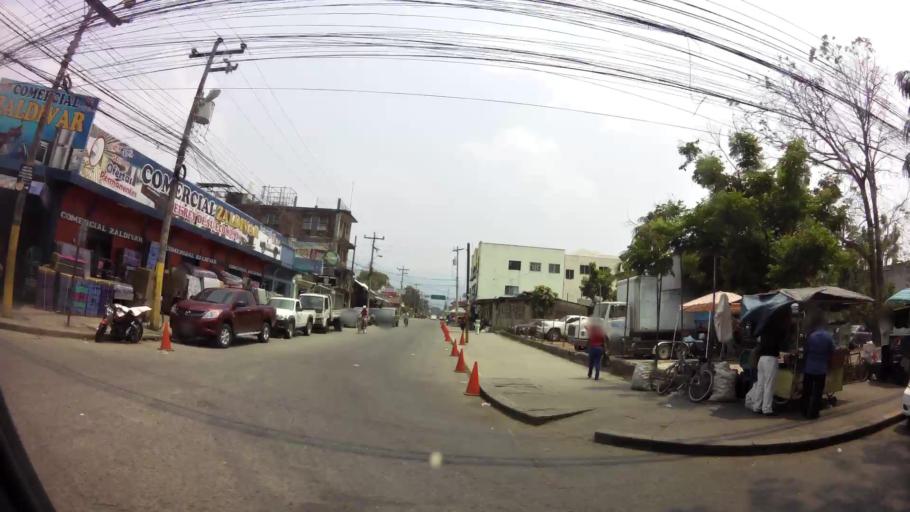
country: HN
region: Yoro
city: El Progreso
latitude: 15.4011
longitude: -87.8069
